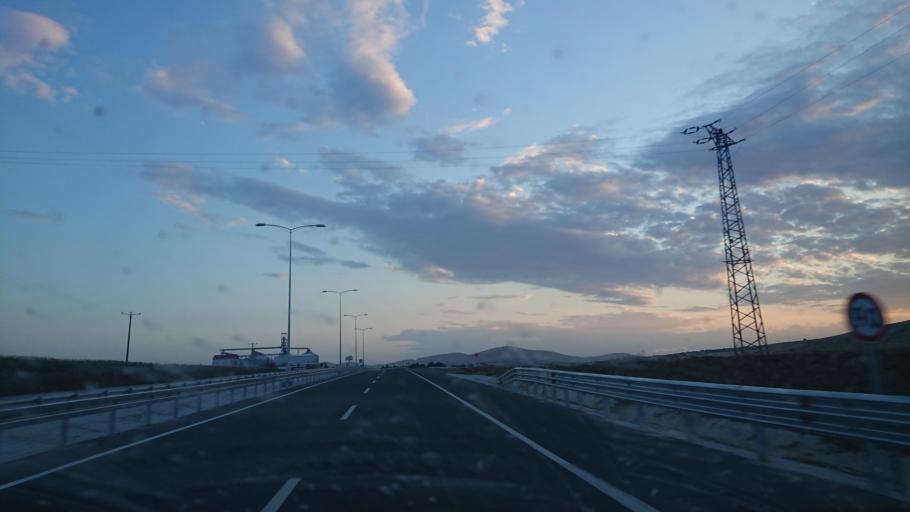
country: TR
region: Aksaray
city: Balci
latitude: 38.7684
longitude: 34.0976
